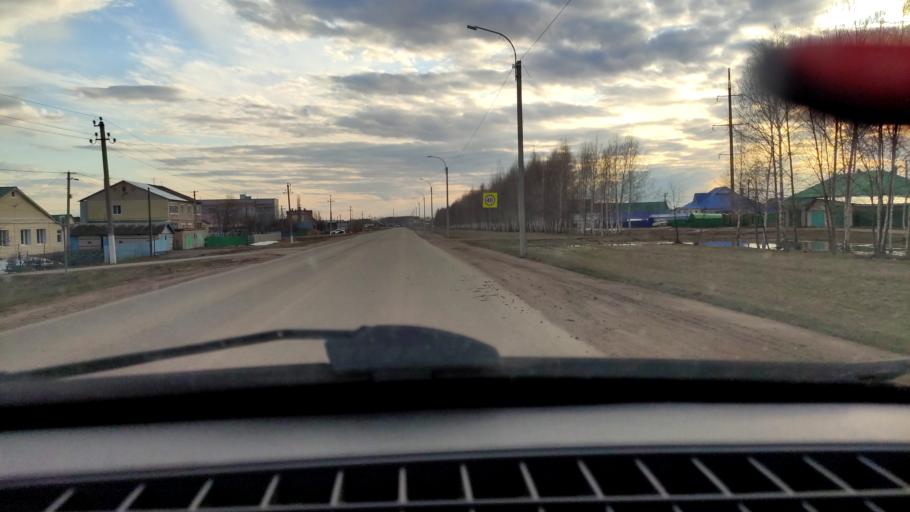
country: RU
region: Bashkortostan
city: Tolbazy
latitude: 54.0045
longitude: 55.8664
